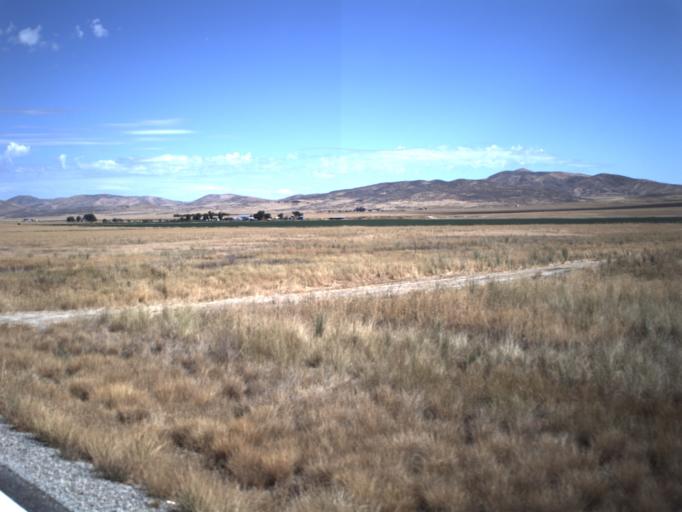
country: US
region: Utah
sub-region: Box Elder County
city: Tremonton
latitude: 41.7270
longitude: -112.4338
